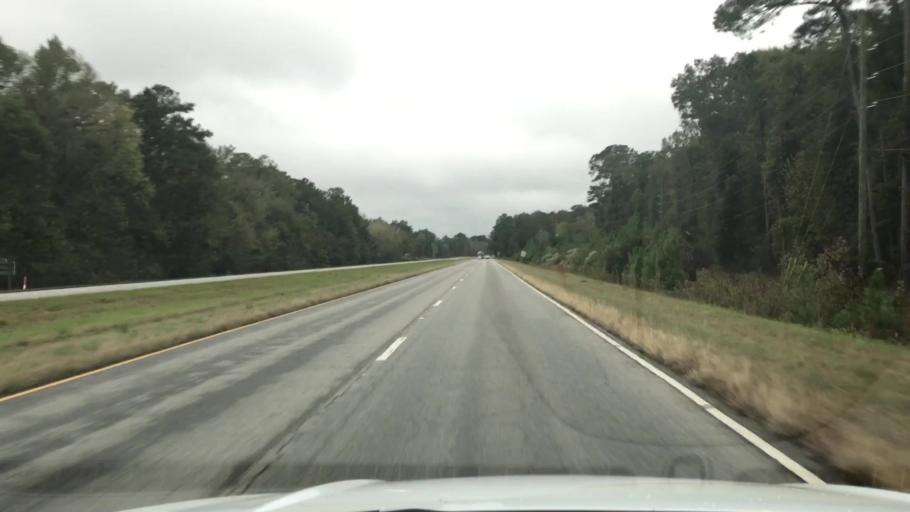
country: US
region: South Carolina
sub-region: Charleston County
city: Ravenel
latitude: 32.7628
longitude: -80.4309
